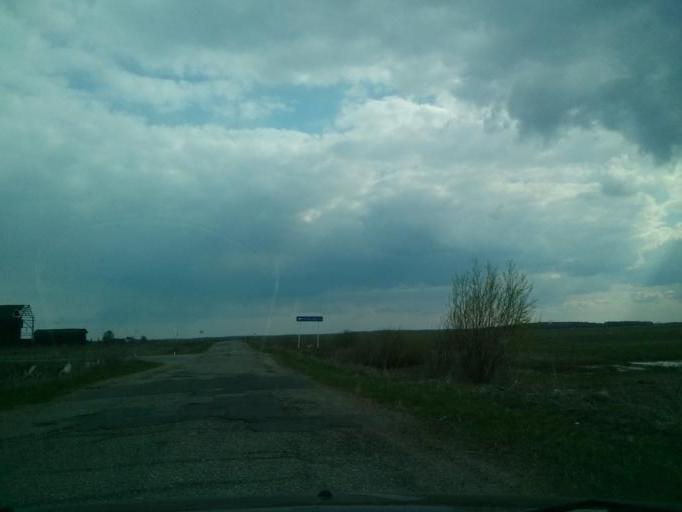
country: RU
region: Vladimir
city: Melenki
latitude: 55.3179
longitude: 41.7797
